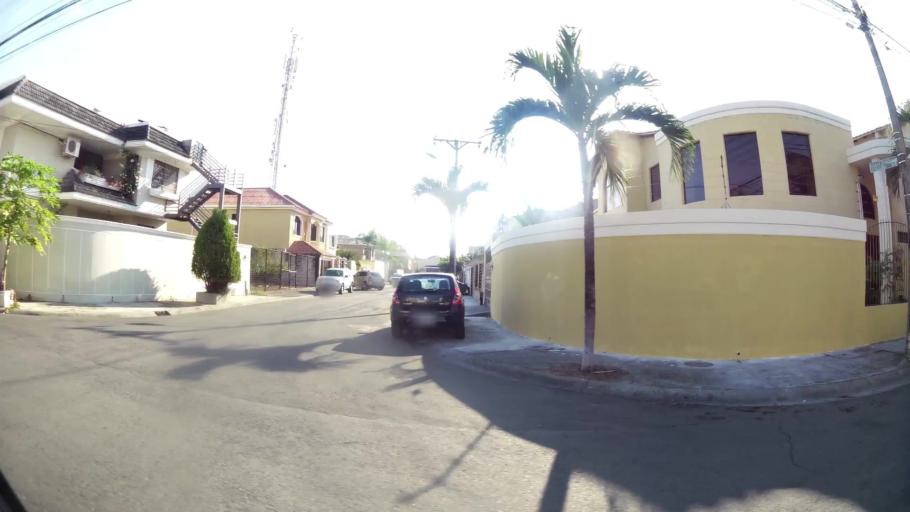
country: EC
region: Guayas
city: Santa Lucia
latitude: -2.1895
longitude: -79.9717
